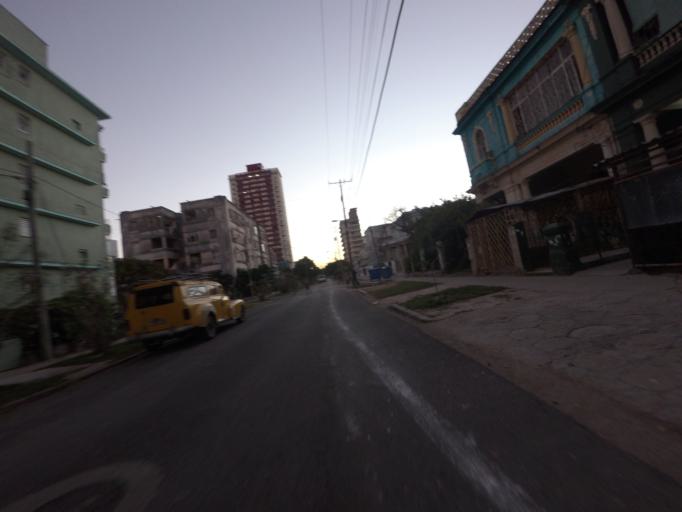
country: CU
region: La Habana
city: Havana
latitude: 23.1436
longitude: -82.3895
